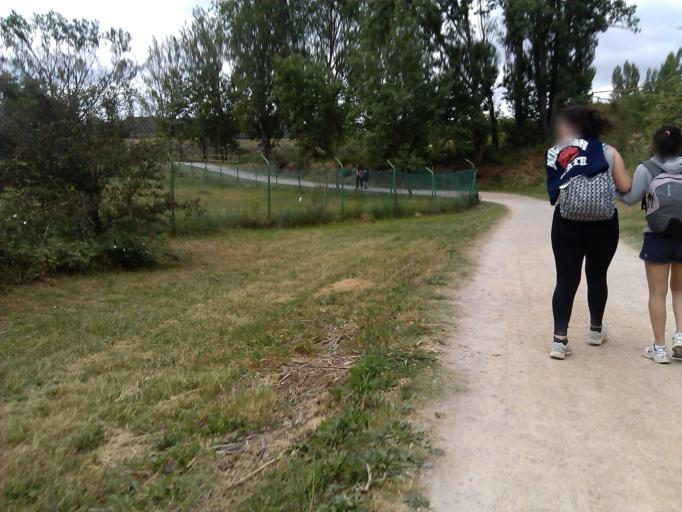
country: ES
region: La Rioja
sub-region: Provincia de La Rioja
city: Navarrete
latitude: 42.4435
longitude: -2.5129
